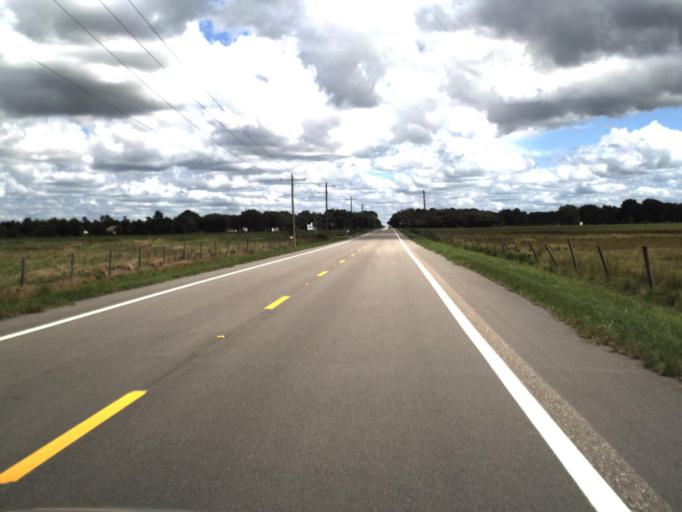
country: US
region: Florida
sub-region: Polk County
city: Crooked Lake Park
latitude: 27.7334
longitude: -81.6479
